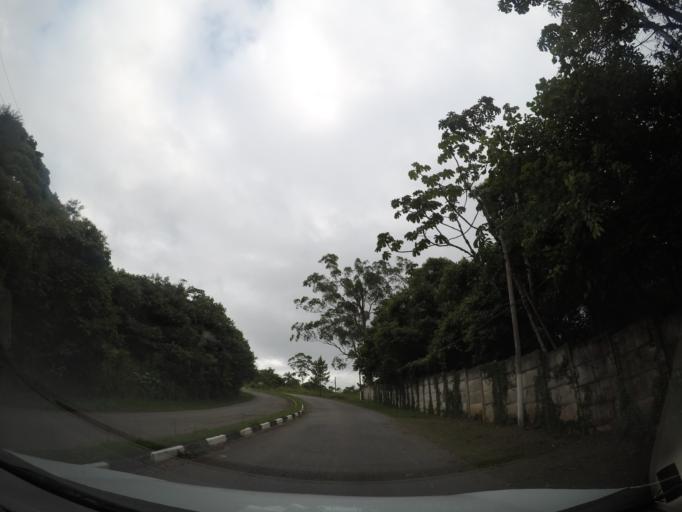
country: BR
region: Sao Paulo
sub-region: Aruja
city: Aruja
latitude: -23.3763
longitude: -46.3630
